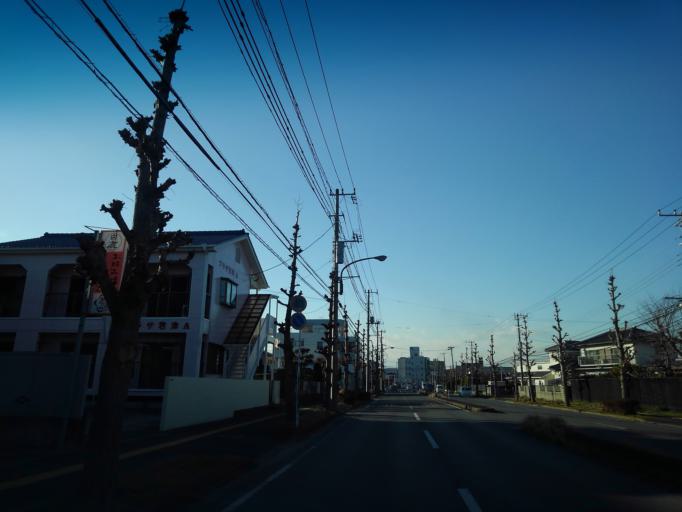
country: JP
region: Chiba
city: Kimitsu
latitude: 35.3330
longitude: 139.9010
